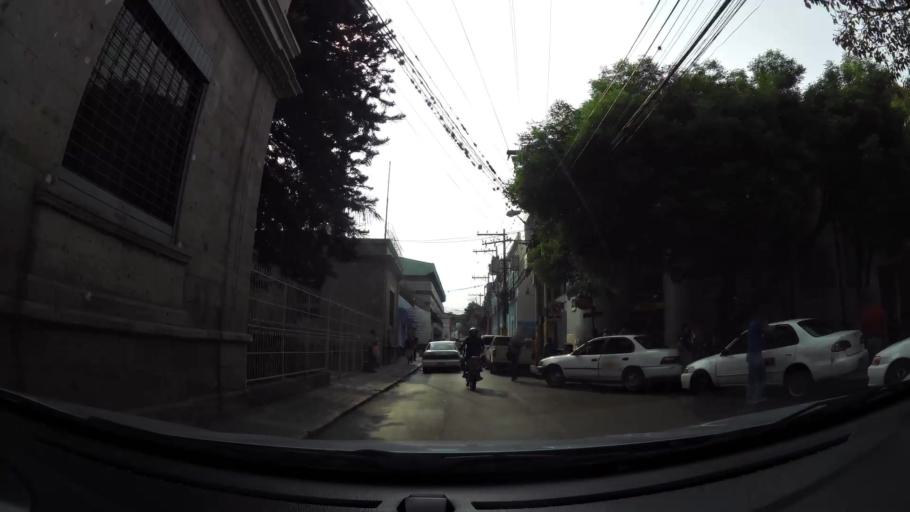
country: HN
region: Francisco Morazan
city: Tegucigalpa
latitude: 14.1062
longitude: -87.2044
